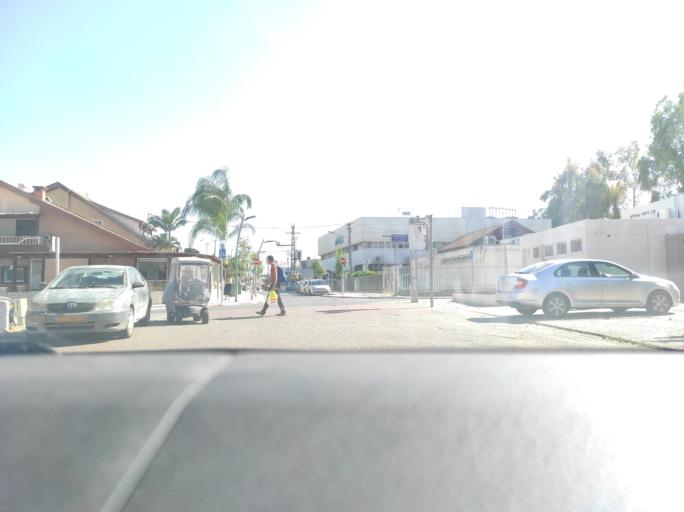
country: IL
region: Southern District
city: Sederot
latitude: 31.5240
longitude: 34.5967
